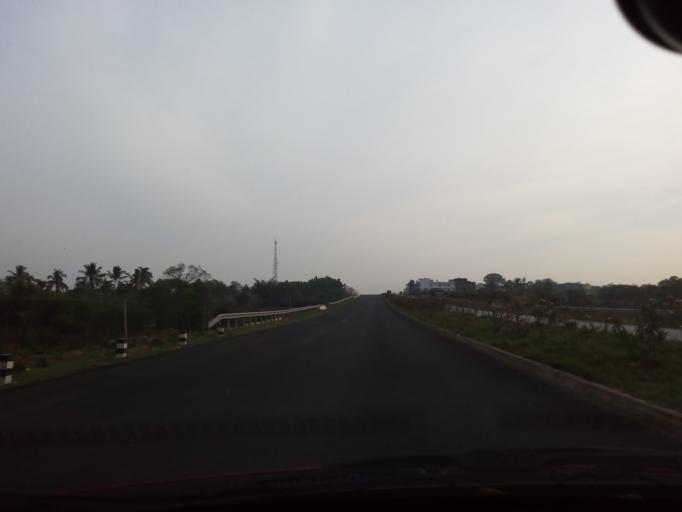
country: IN
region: Karnataka
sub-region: Chikkaballapur
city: Gudibanda
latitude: 13.5828
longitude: 77.7825
